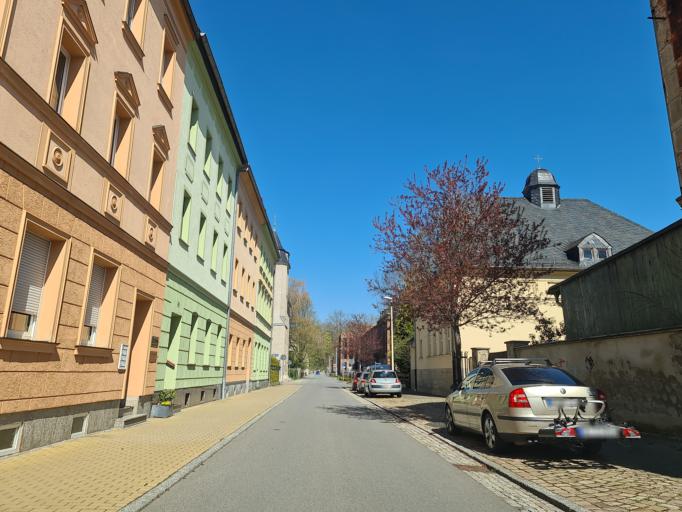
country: DE
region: Saxony
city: Glauchau
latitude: 50.8206
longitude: 12.5378
